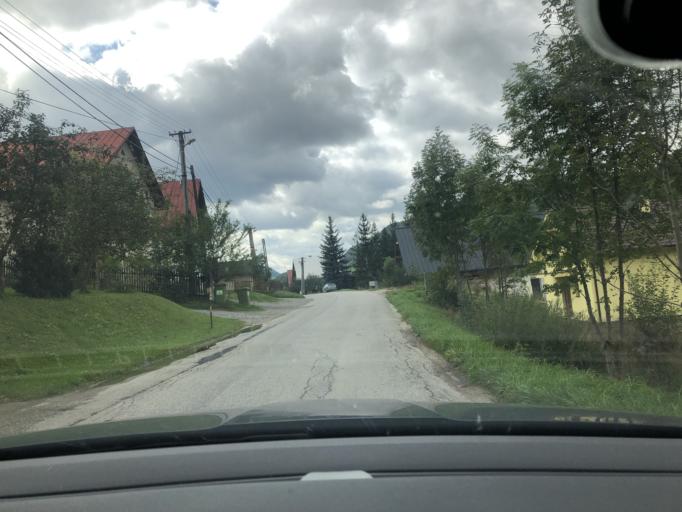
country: SK
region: Zilinsky
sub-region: Okres Zilina
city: Terchova
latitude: 49.2811
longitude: 19.0522
